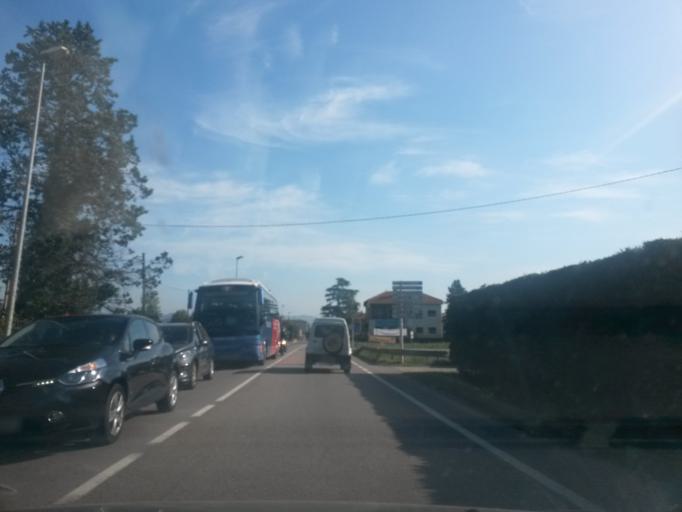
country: ES
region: Catalonia
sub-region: Provincia de Girona
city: Bas
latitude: 42.1412
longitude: 2.4569
